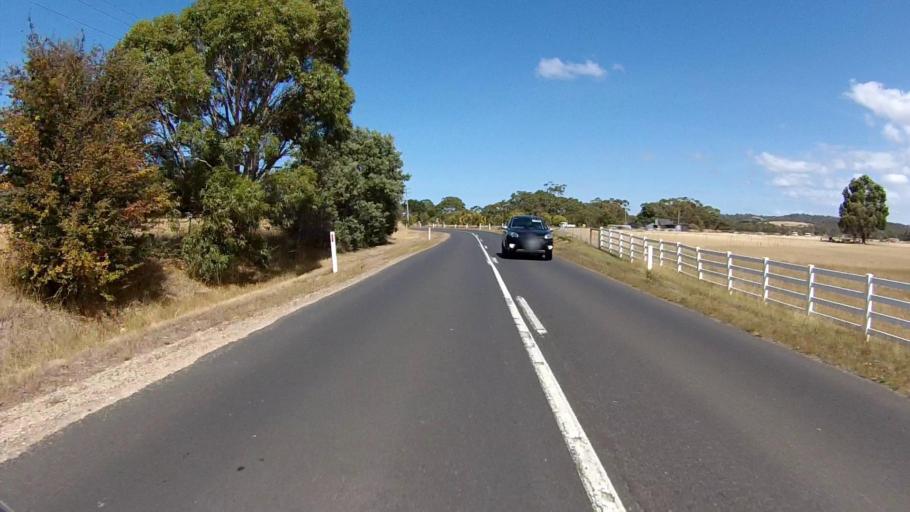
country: AU
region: Tasmania
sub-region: Break O'Day
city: St Helens
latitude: -42.1128
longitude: 148.0560
